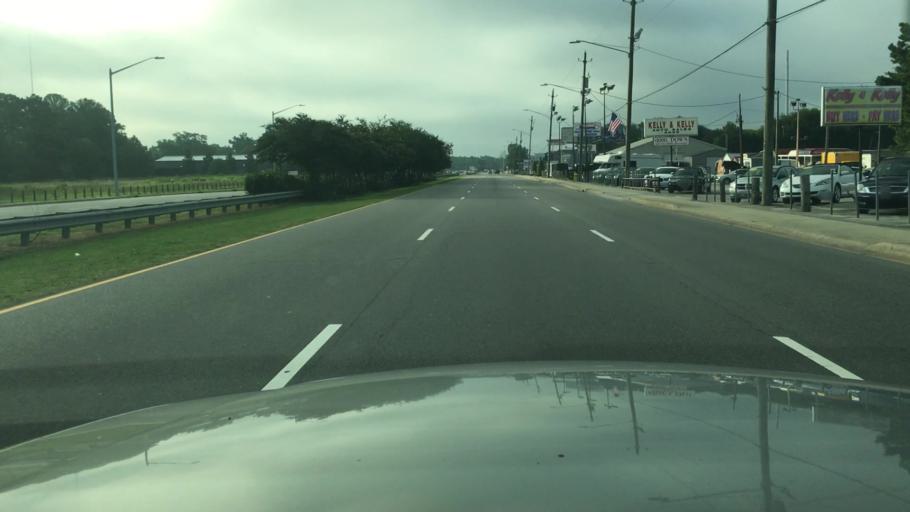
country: US
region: North Carolina
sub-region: Cumberland County
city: Fayetteville
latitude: 35.0829
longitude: -78.9460
